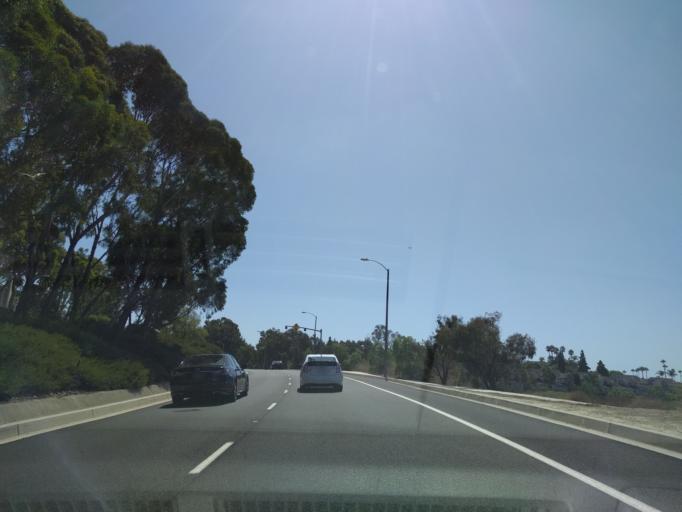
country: US
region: California
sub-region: Orange County
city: Laguna Niguel
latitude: 33.4980
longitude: -117.7120
